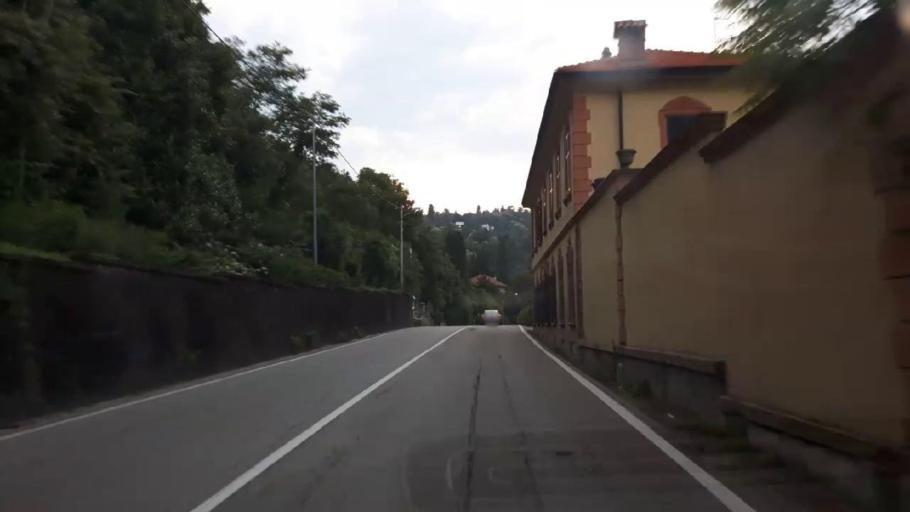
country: IT
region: Piedmont
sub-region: Provincia di Novara
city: Arona
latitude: 45.7709
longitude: 8.5465
